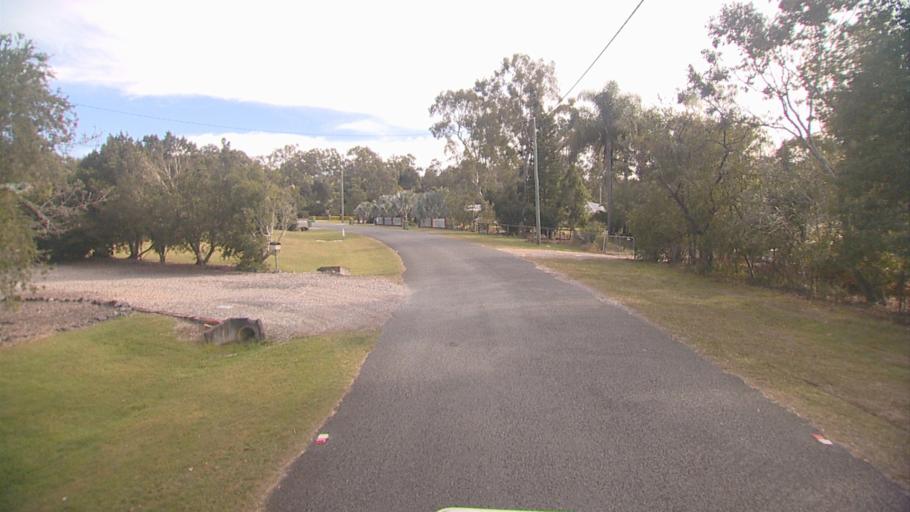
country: AU
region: Queensland
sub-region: Logan
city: Park Ridge South
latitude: -27.7380
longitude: 153.0368
